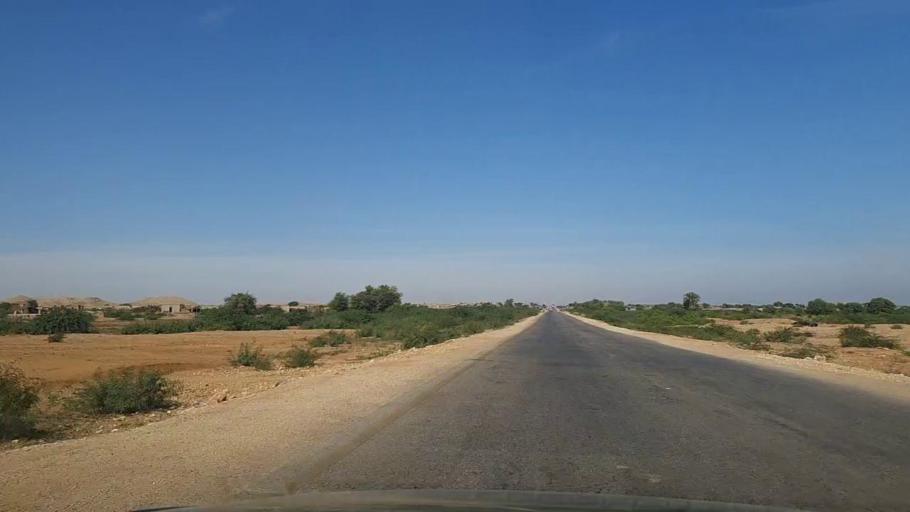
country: PK
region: Sindh
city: Kotri
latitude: 25.1747
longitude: 68.2397
